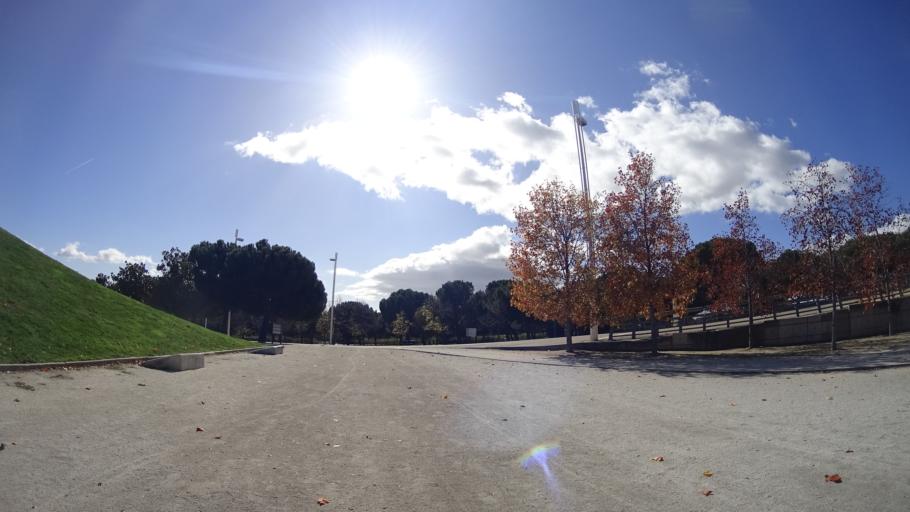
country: ES
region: Madrid
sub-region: Provincia de Madrid
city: San Blas
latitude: 40.4587
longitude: -3.6076
